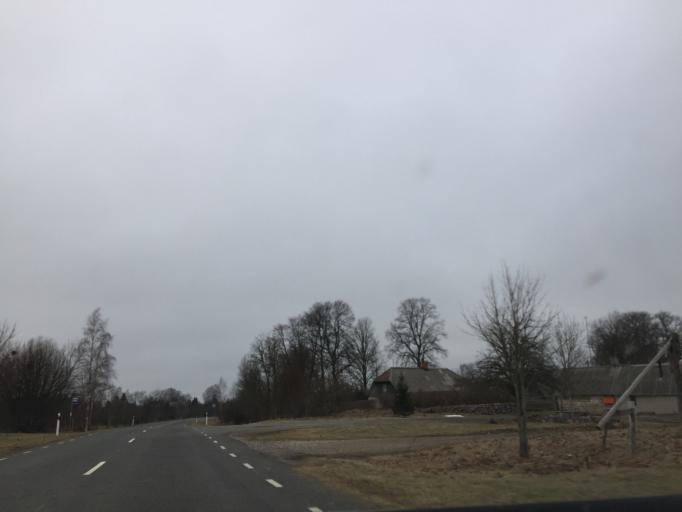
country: EE
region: Saare
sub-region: Kuressaare linn
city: Kuressaare
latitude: 58.5371
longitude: 22.3387
